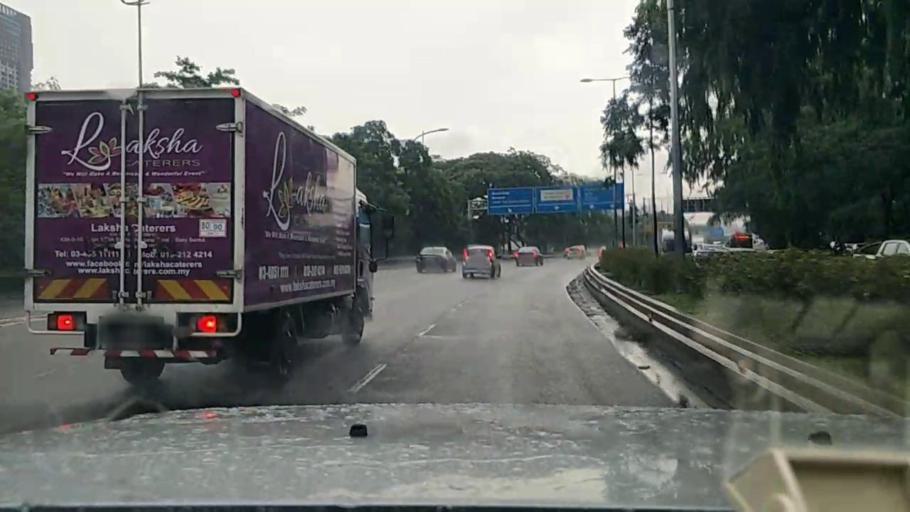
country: MY
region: Kuala Lumpur
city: Kuala Lumpur
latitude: 3.1218
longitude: 101.6800
